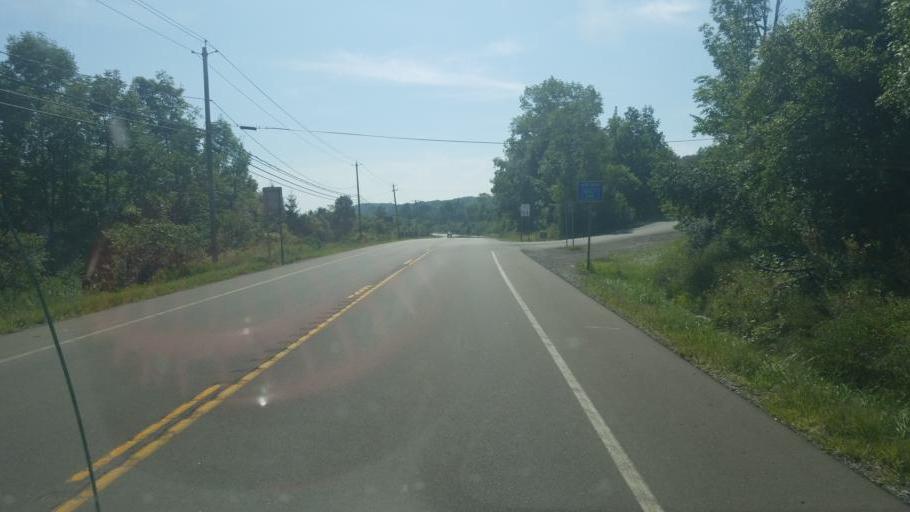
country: US
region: New York
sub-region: Allegany County
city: Wellsville
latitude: 42.0999
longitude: -78.0439
